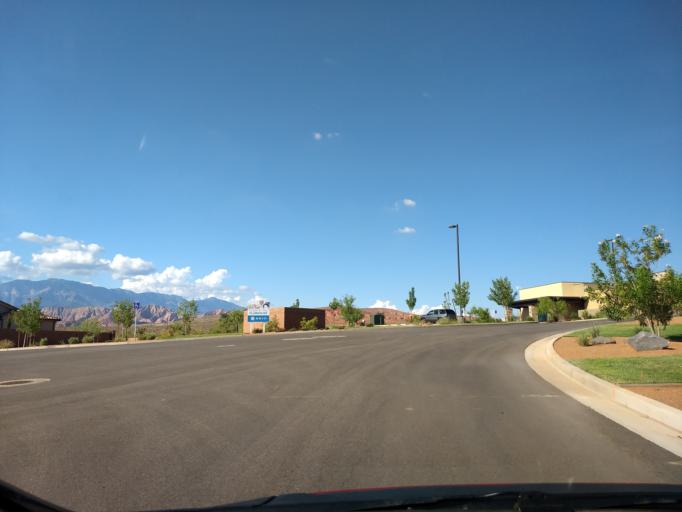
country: US
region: Utah
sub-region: Washington County
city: Washington
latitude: 37.1426
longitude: -113.5145
